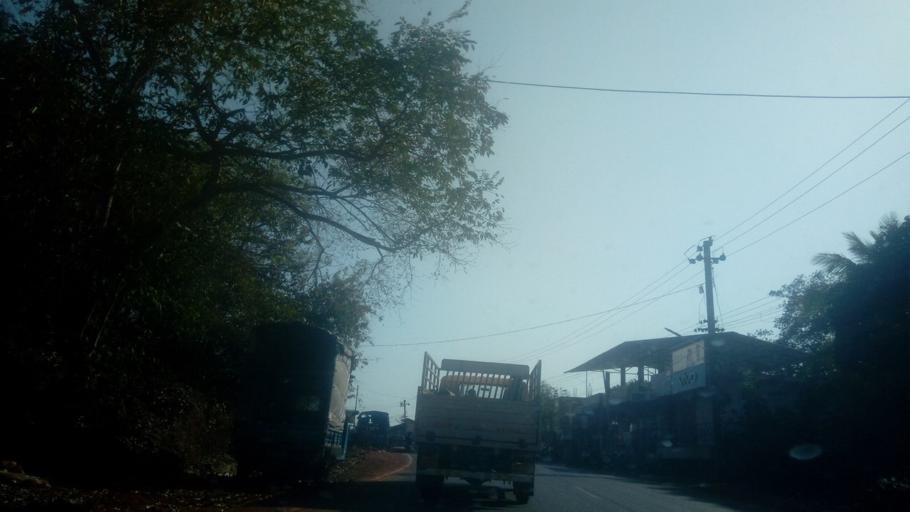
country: IN
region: Goa
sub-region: North Goa
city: Jua
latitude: 15.4935
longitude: 73.9572
